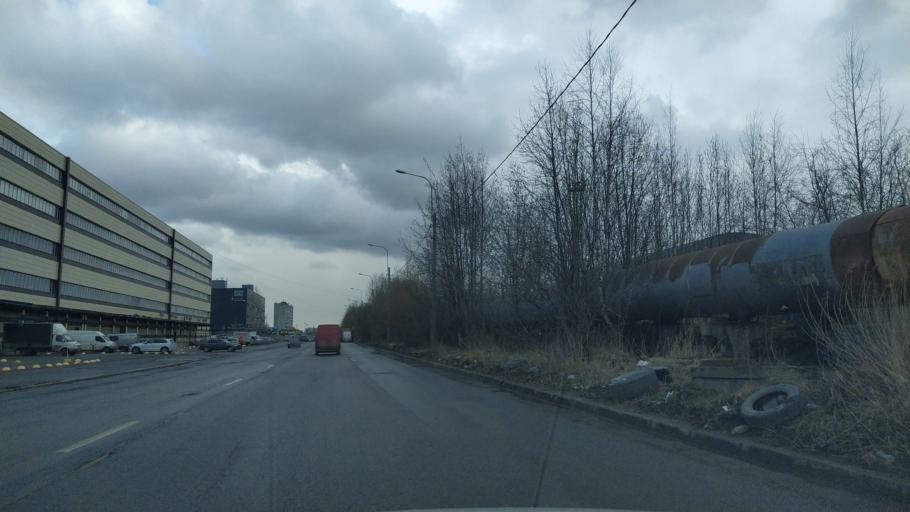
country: RU
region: Leningrad
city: Parnas
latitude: 60.0570
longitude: 30.3666
